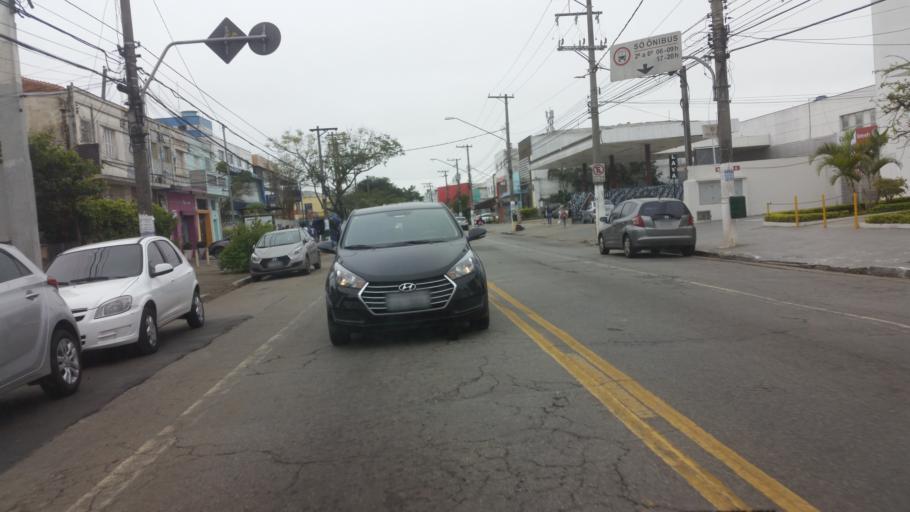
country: BR
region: Sao Paulo
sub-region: Sao Caetano Do Sul
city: Sao Caetano do Sul
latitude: -23.6161
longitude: -46.6177
